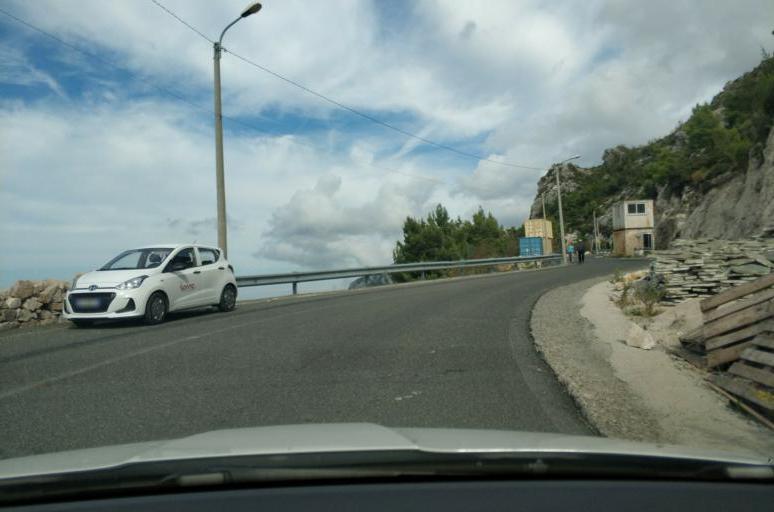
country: AL
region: Durres
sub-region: Rrethi i Krujes
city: Kruje
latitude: 41.5224
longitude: 19.7934
